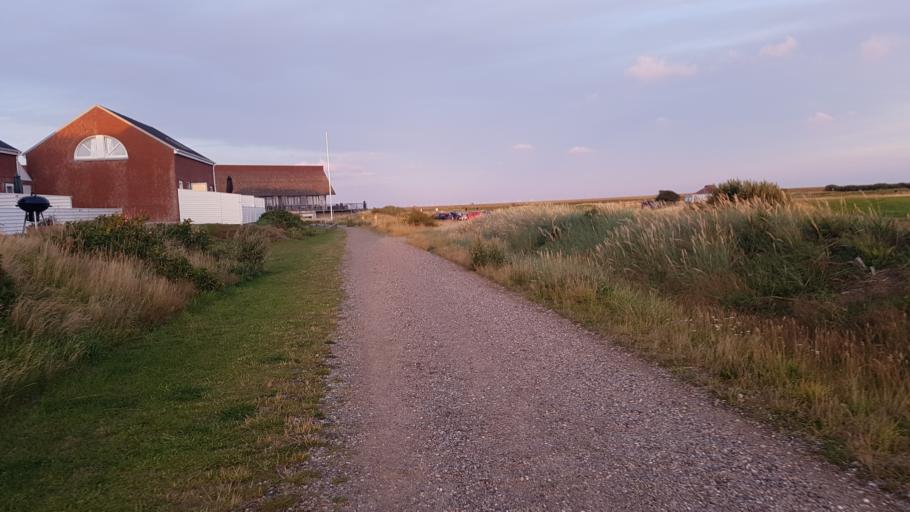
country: DE
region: Schleswig-Holstein
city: List
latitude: 55.0852
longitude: 8.5496
